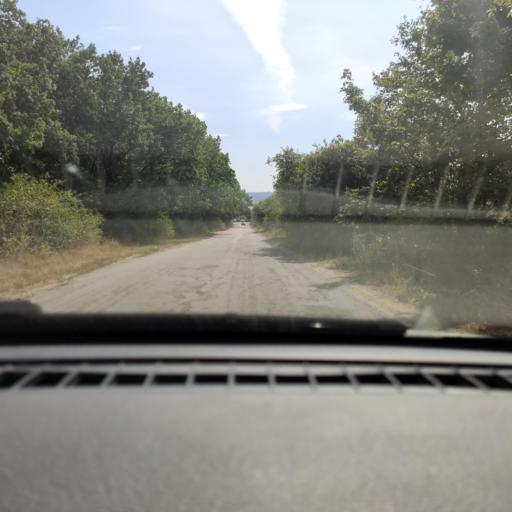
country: RU
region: Voronezj
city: Pridonskoy
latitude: 51.7369
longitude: 39.0591
